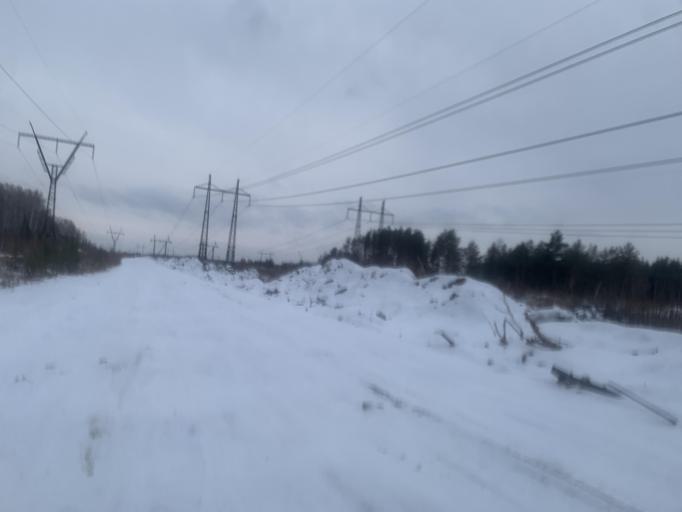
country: RU
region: Chelyabinsk
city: Roshchino
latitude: 55.1964
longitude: 61.2611
